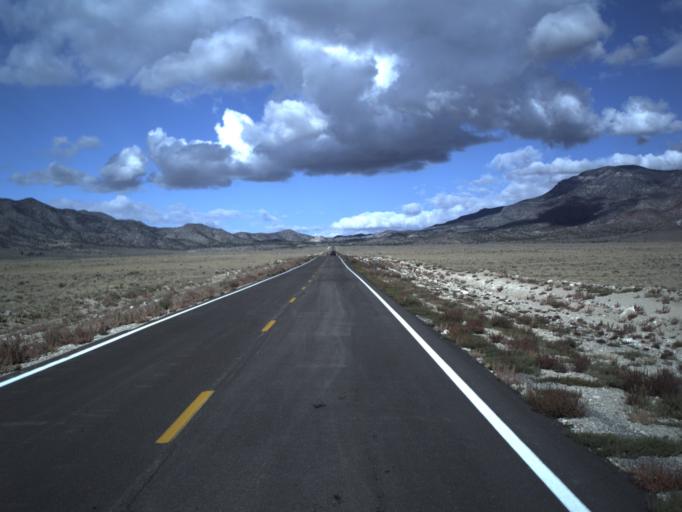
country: US
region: Utah
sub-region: Beaver County
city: Milford
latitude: 38.4867
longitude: -113.4567
